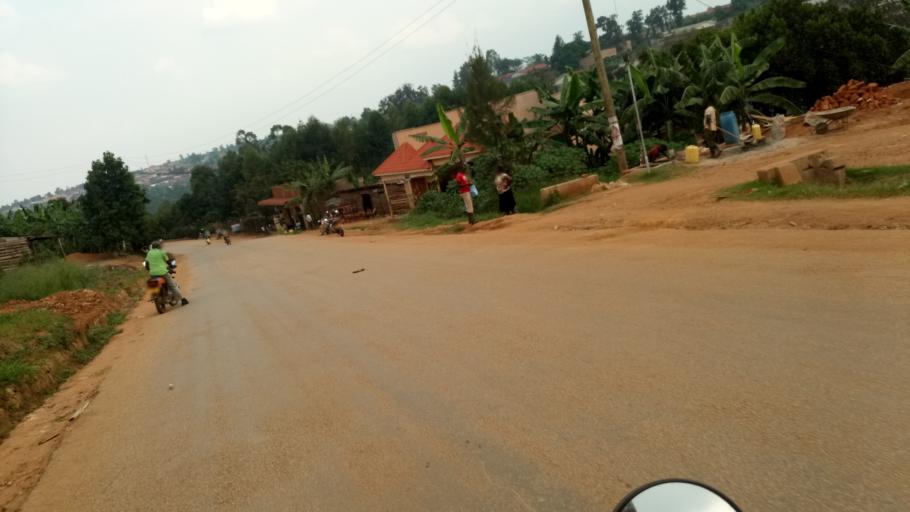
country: UG
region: Western Region
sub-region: Mbarara District
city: Mbarara
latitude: -0.6109
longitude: 30.6643
